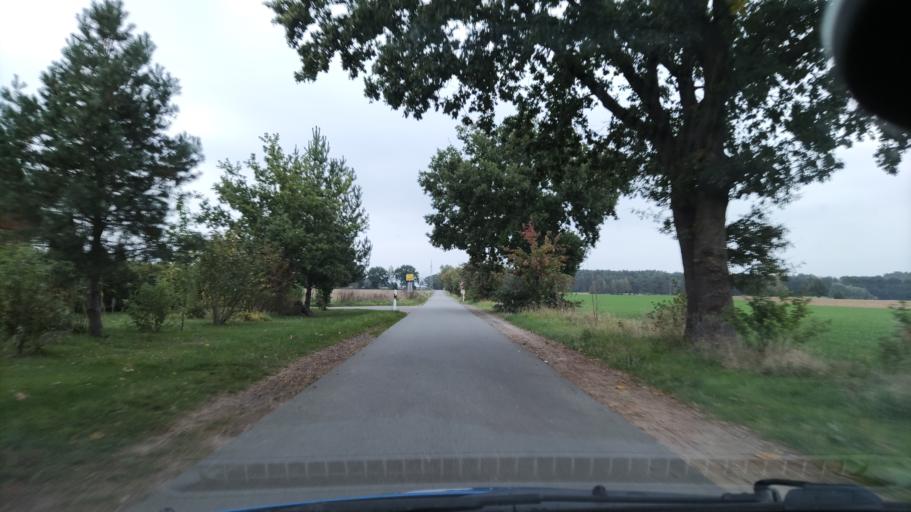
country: DE
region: Lower Saxony
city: Karwitz
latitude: 53.0921
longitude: 11.0138
